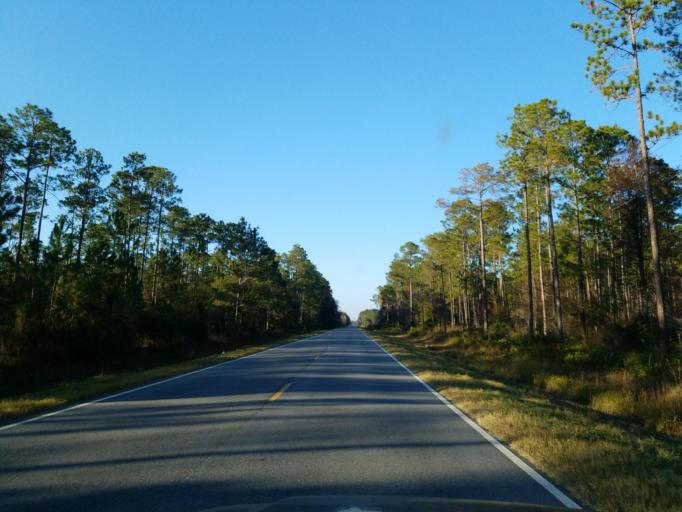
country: US
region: Georgia
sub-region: Lanier County
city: Lakeland
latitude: 31.1069
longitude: -83.0807
